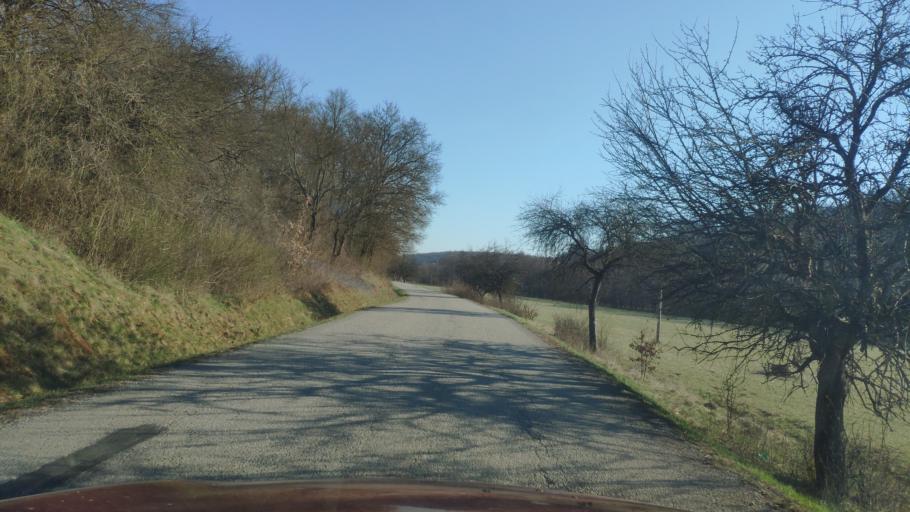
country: SK
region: Banskobystricky
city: Revuca
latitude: 48.5350
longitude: 20.2449
